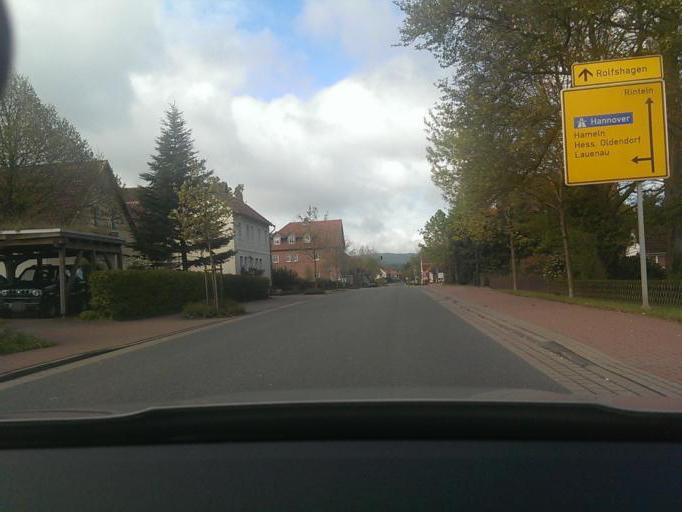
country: DE
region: Lower Saxony
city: Rehren
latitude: 52.2338
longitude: 9.2381
